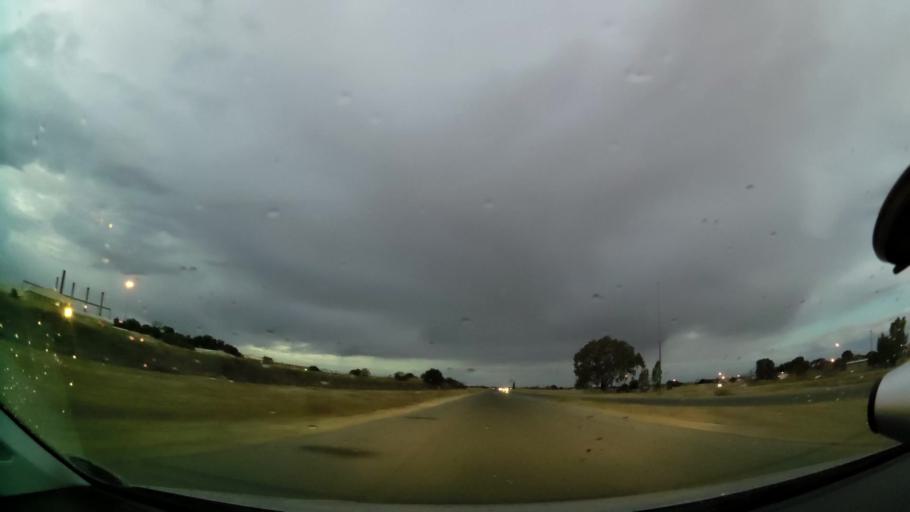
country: ZA
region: Orange Free State
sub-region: Lejweleputswa District Municipality
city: Welkom
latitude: -27.9537
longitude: 26.7881
